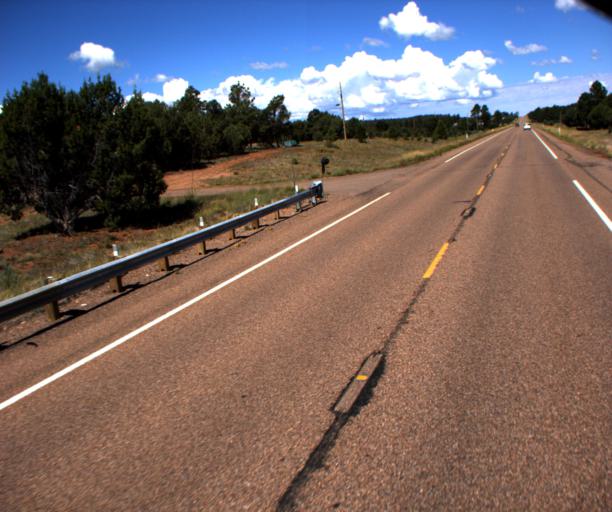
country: US
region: Arizona
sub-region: Navajo County
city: Linden
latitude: 34.3251
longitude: -110.2572
